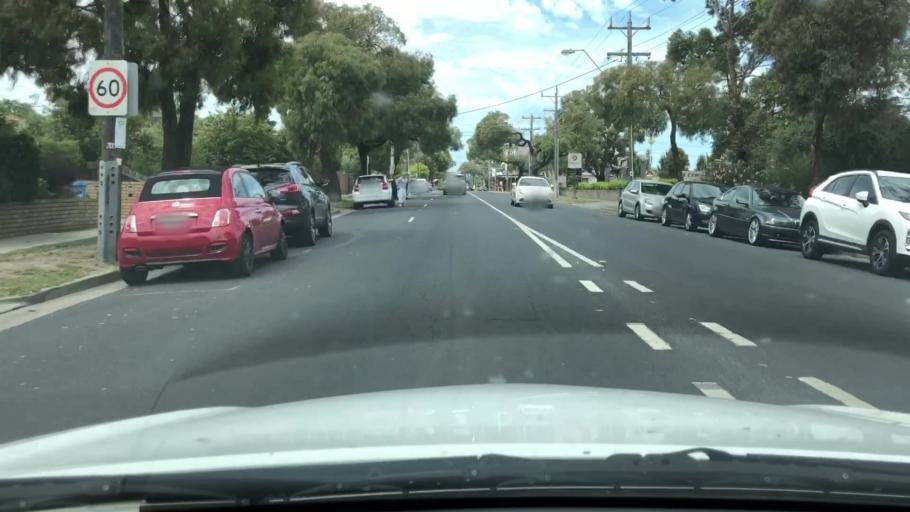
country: AU
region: Victoria
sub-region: Bayside
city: Black Rock
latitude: -37.9605
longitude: 145.0193
